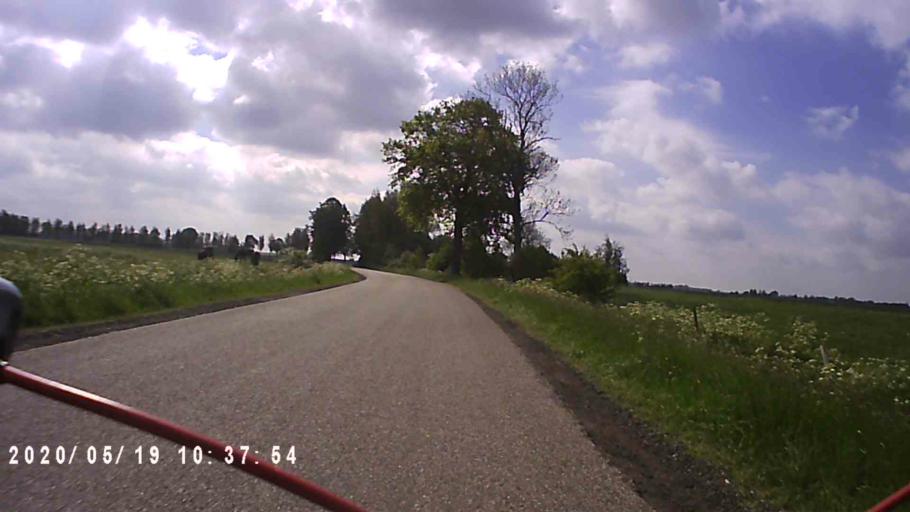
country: NL
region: Friesland
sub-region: Gemeente Kollumerland en Nieuwkruisland
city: Kollum
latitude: 53.2734
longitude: 6.1864
